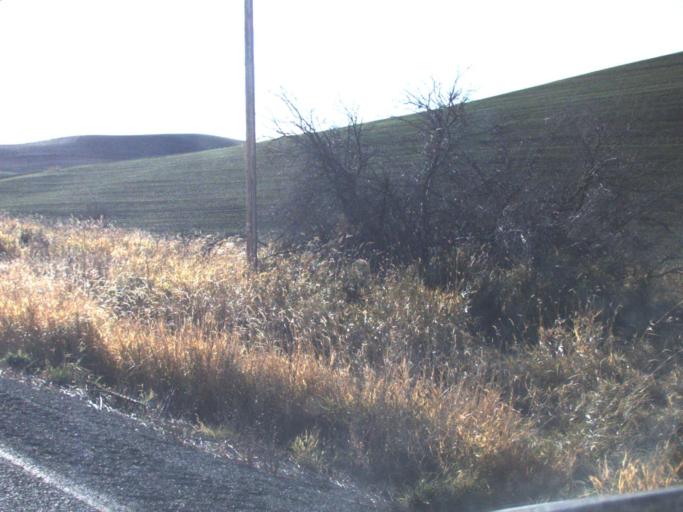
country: US
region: Washington
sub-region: Whitman County
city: Colfax
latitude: 46.7651
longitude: -117.3893
